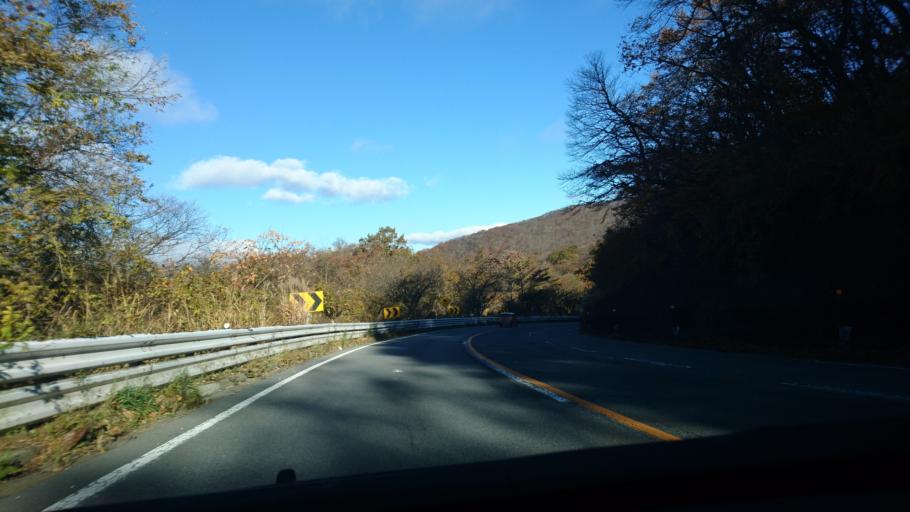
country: JP
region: Nagano
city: Saku
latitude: 36.3229
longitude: 138.6486
